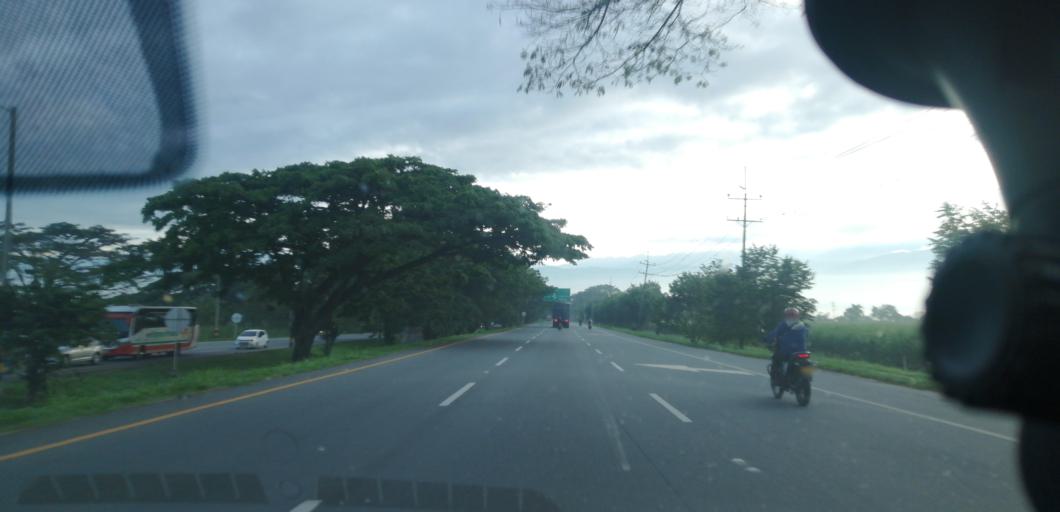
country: CO
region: Valle del Cauca
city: Palmira
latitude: 3.5233
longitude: -76.3427
